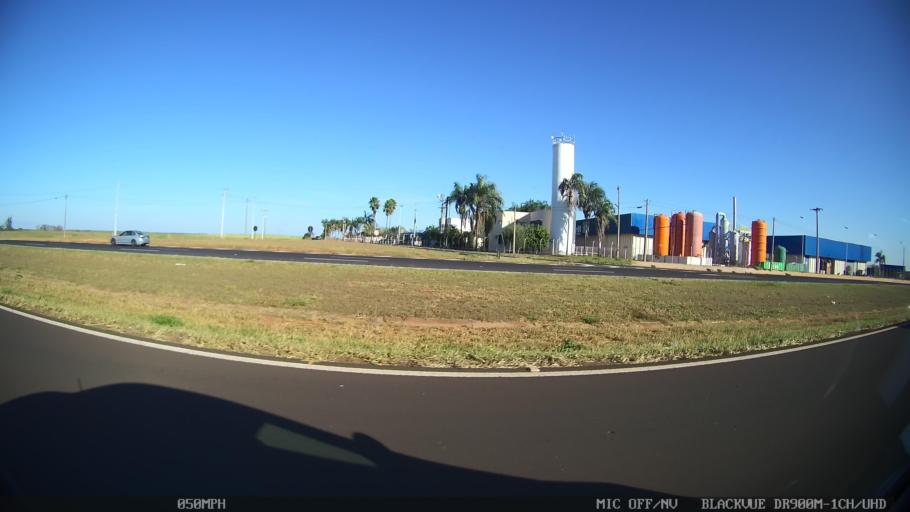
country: BR
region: Sao Paulo
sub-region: Olimpia
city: Olimpia
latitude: -20.7162
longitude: -48.9984
